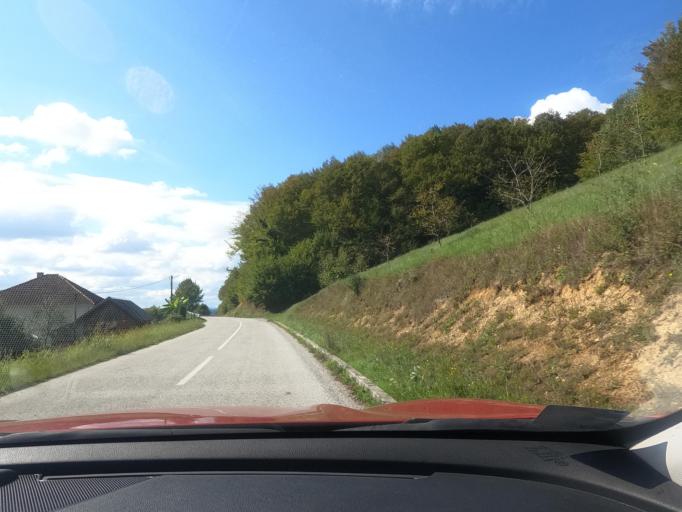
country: BA
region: Federation of Bosnia and Herzegovina
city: Velika Kladusa
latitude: 45.2234
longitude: 15.8345
